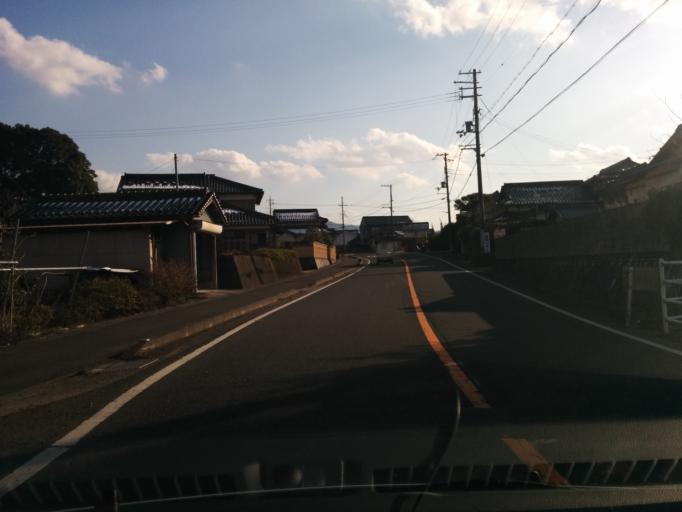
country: JP
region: Kyoto
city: Ayabe
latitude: 35.3299
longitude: 135.2150
